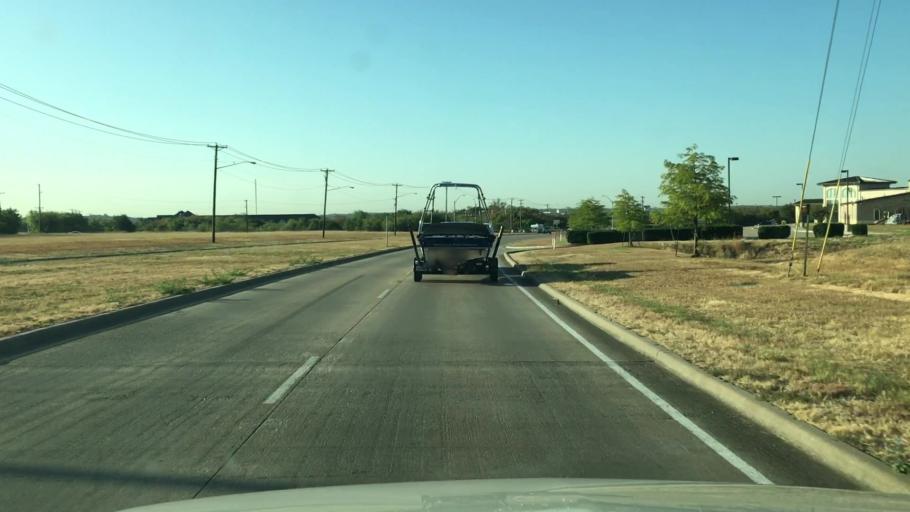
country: US
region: Texas
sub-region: Johnson County
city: Burleson
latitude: 32.5323
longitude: -97.3537
